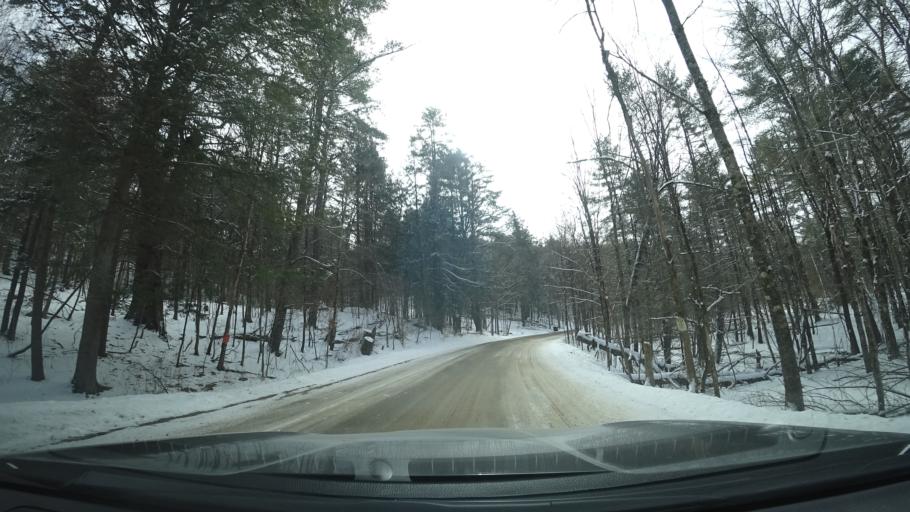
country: US
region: New York
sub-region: Washington County
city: Greenwich
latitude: 43.2248
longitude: -73.3558
